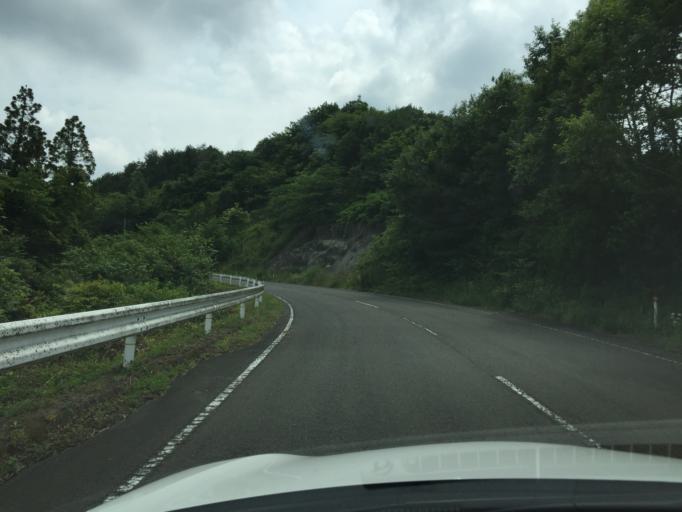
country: JP
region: Fukushima
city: Sukagawa
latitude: 37.2703
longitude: 140.5015
